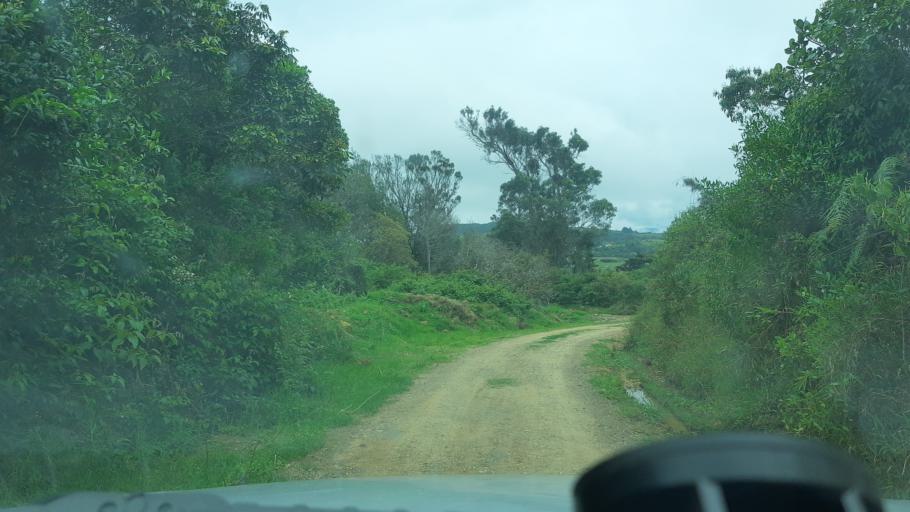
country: CO
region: Boyaca
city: Santa Sofia
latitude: 5.7128
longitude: -73.5904
